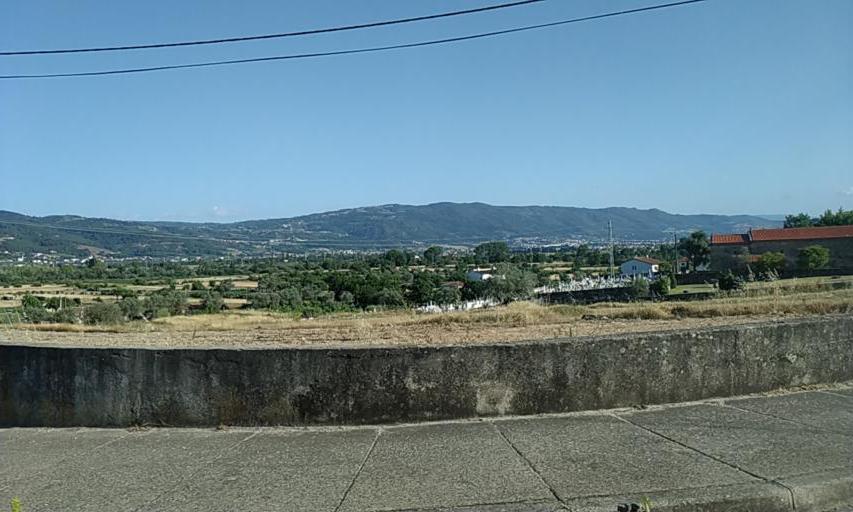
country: PT
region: Vila Real
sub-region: Chaves
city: Chaves
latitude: 41.7697
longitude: -7.4499
